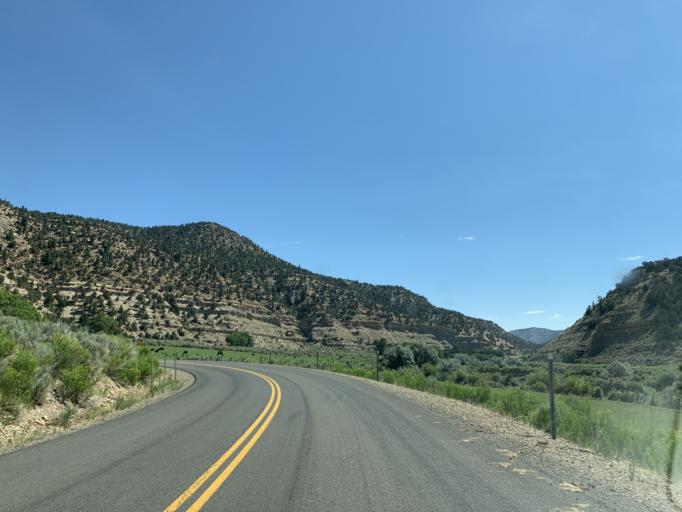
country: US
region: Utah
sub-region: Carbon County
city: East Carbon City
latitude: 39.7756
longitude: -110.4546
